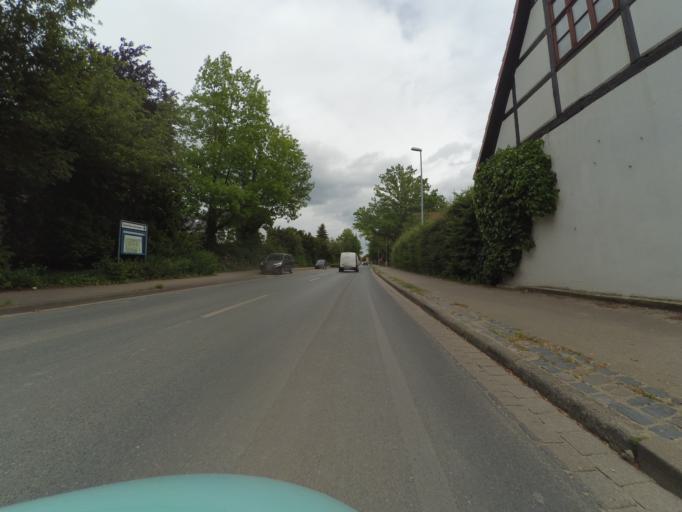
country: DE
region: Lower Saxony
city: Isernhagen Farster Bauerschaft
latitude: 52.4564
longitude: 9.8027
